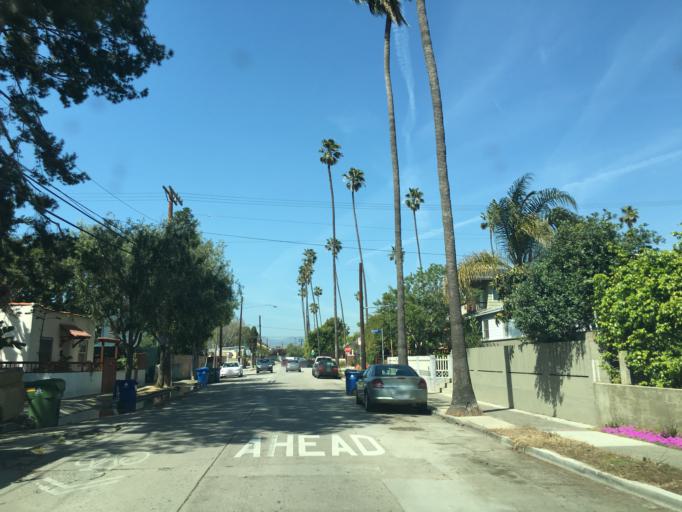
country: US
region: California
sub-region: Los Angeles County
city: Marina del Rey
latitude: 33.9939
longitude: -118.4614
